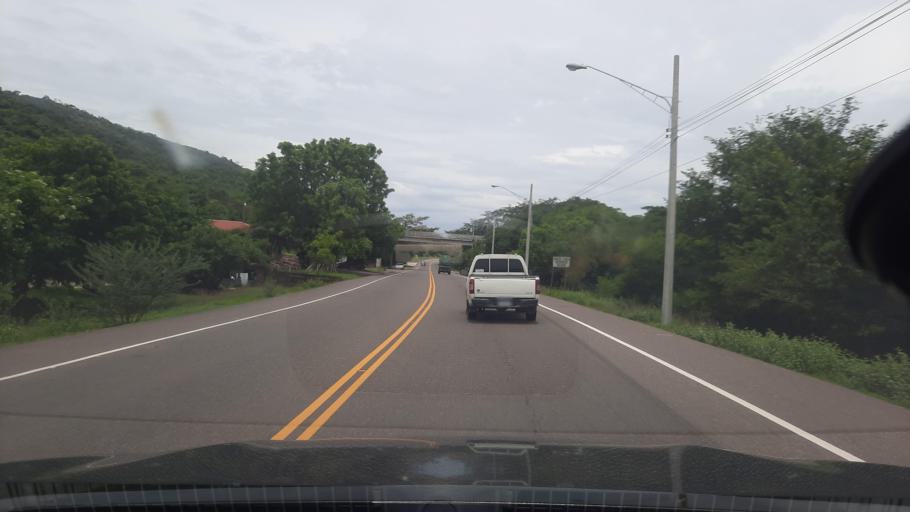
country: HN
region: Valle
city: Langue
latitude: 13.5912
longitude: -87.6966
